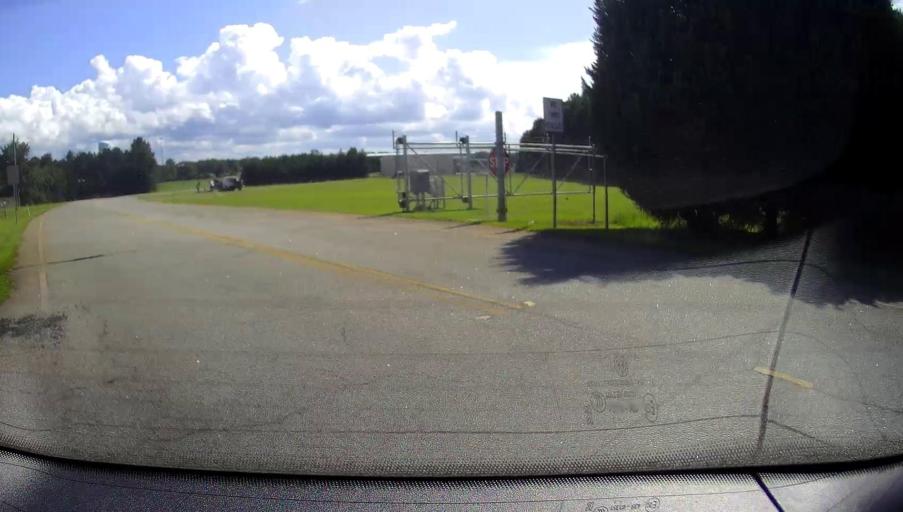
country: US
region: Georgia
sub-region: Upson County
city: Hannahs Mill
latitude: 32.9453
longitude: -84.3382
